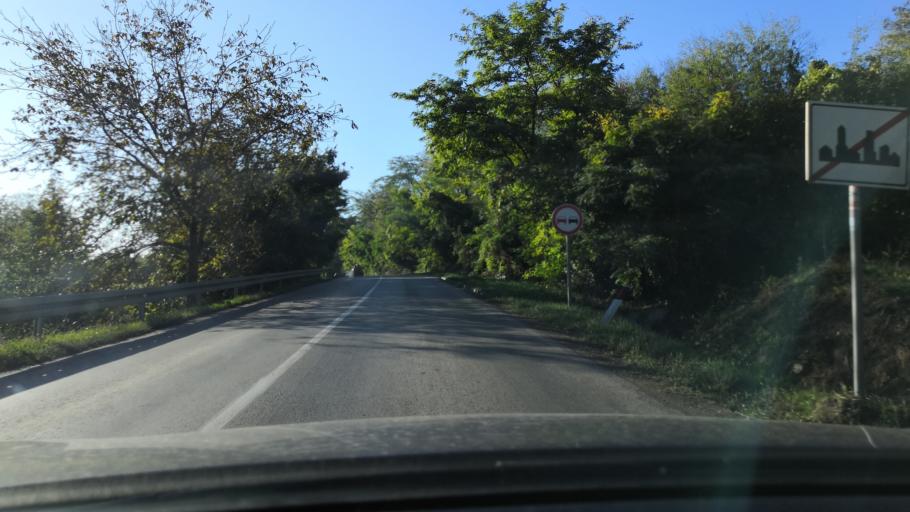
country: RS
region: Autonomna Pokrajina Vojvodina
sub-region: Juznobacki Okrug
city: Petrovaradin
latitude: 45.2275
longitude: 19.8967
